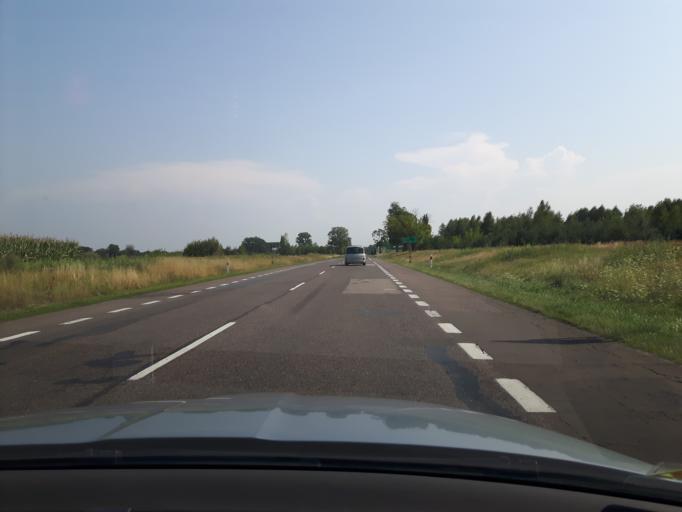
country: PL
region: Masovian Voivodeship
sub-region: Powiat ciechanowski
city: Glinojeck
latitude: 52.7823
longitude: 20.2858
